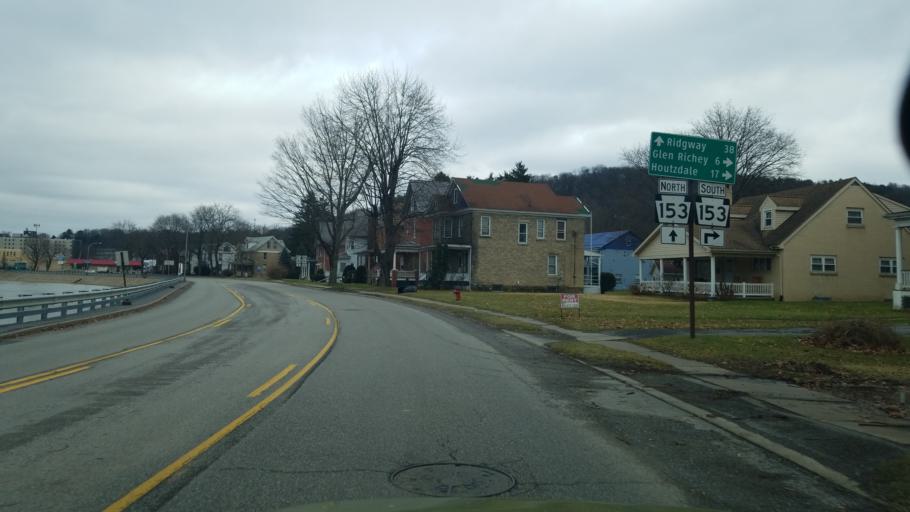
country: US
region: Pennsylvania
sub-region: Clearfield County
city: Clearfield
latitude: 41.0148
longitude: -78.4412
